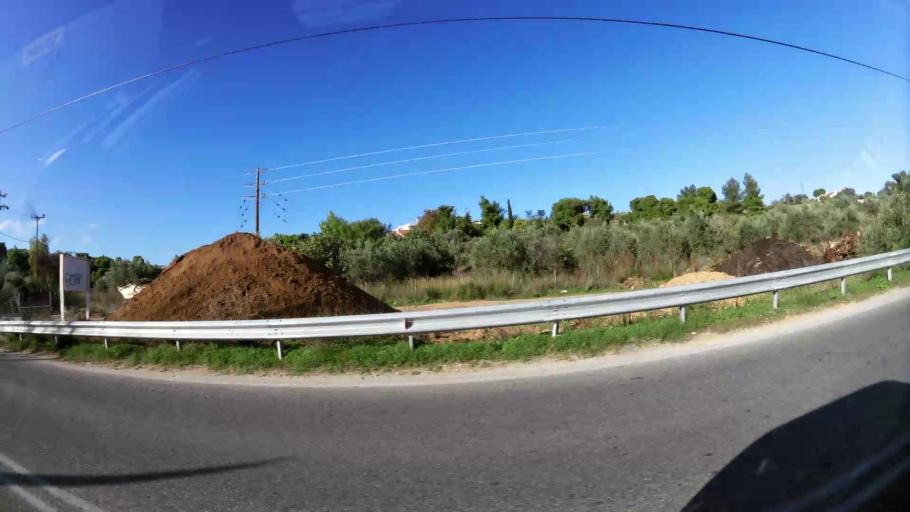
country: GR
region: Attica
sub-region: Nomarchia Anatolikis Attikis
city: Rafina
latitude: 38.0200
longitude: 23.9936
